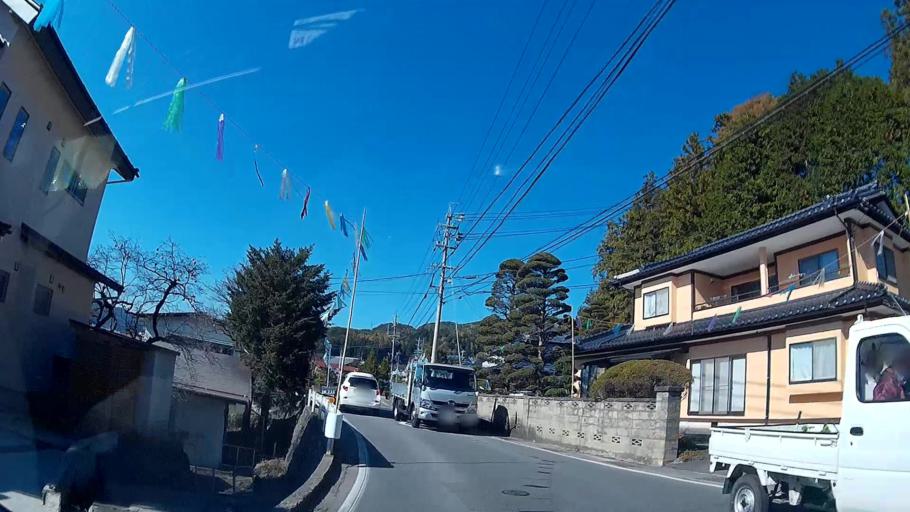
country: JP
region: Nagano
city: Okaya
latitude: 36.0821
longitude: 138.0806
